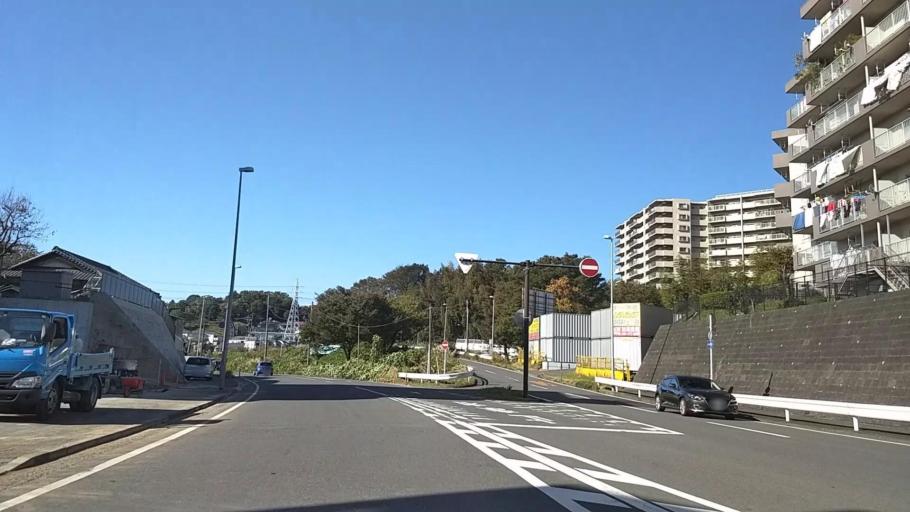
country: JP
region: Kanagawa
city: Fujisawa
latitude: 35.4137
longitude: 139.5359
